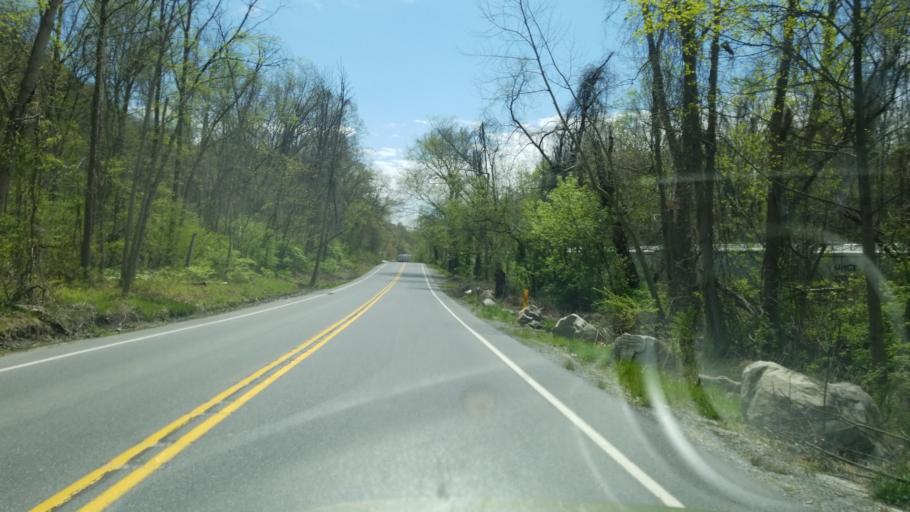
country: US
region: Pennsylvania
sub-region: Huntingdon County
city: Mount Union
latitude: 40.4143
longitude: -77.9324
